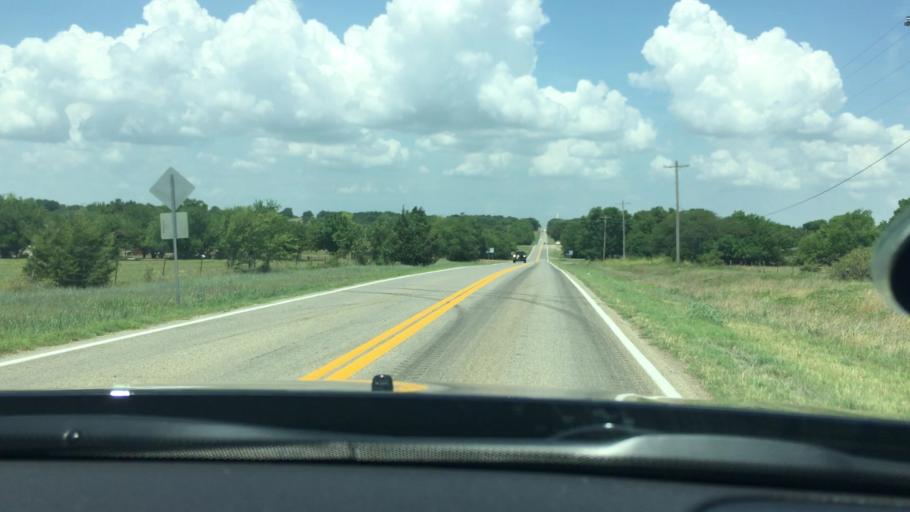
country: US
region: Oklahoma
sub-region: Marshall County
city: Kingston
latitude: 34.0854
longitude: -96.6056
